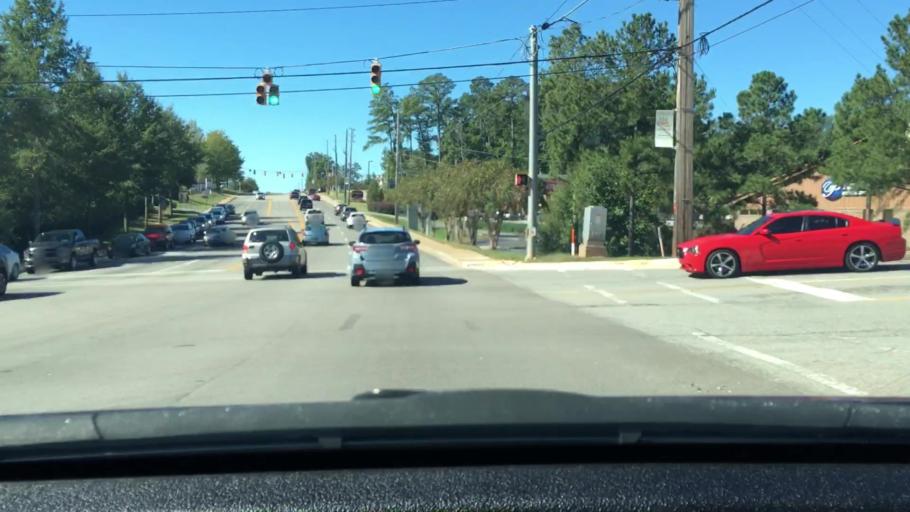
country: US
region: South Carolina
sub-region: Lexington County
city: Irmo
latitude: 34.0909
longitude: -81.1710
